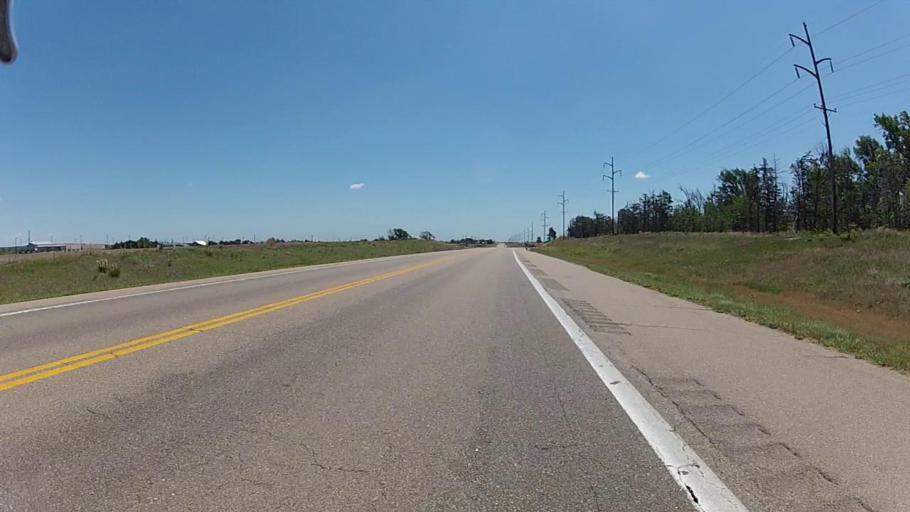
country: US
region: Kansas
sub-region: Ford County
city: Dodge City
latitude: 37.7221
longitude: -100.0370
